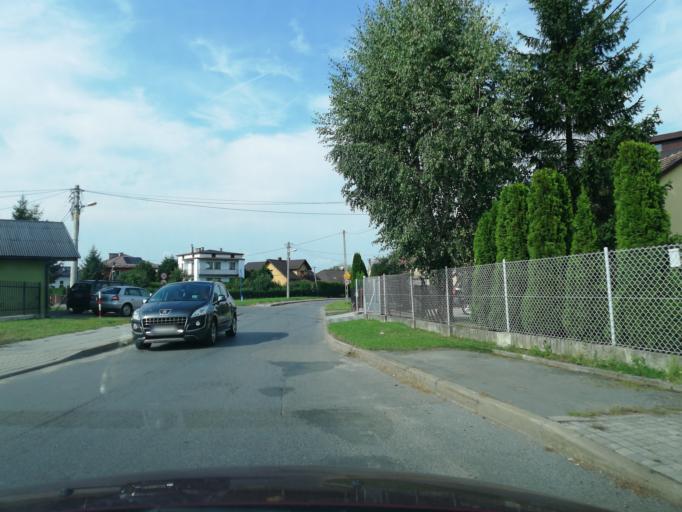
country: PL
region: Lesser Poland Voivodeship
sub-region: Powiat nowosadecki
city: Nowy Sacz
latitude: 49.5946
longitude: 20.7152
